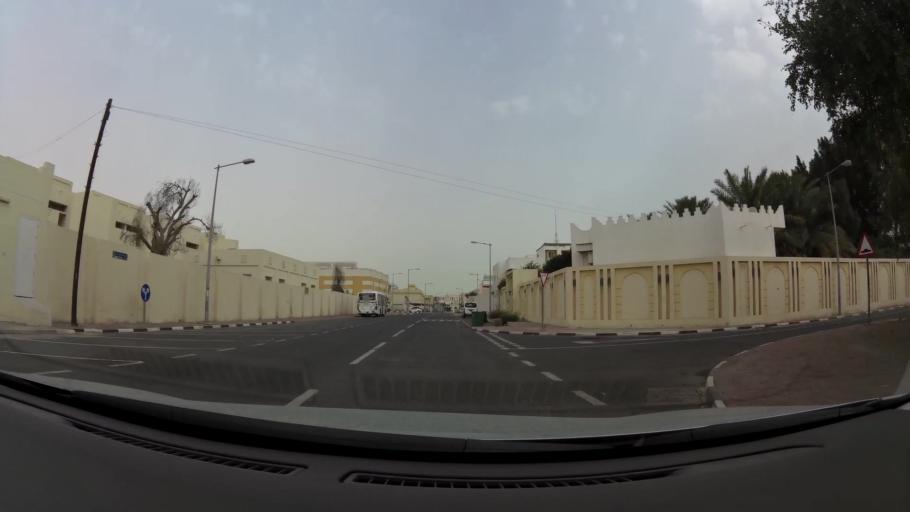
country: QA
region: Baladiyat ad Dawhah
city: Doha
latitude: 25.2576
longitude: 51.5276
